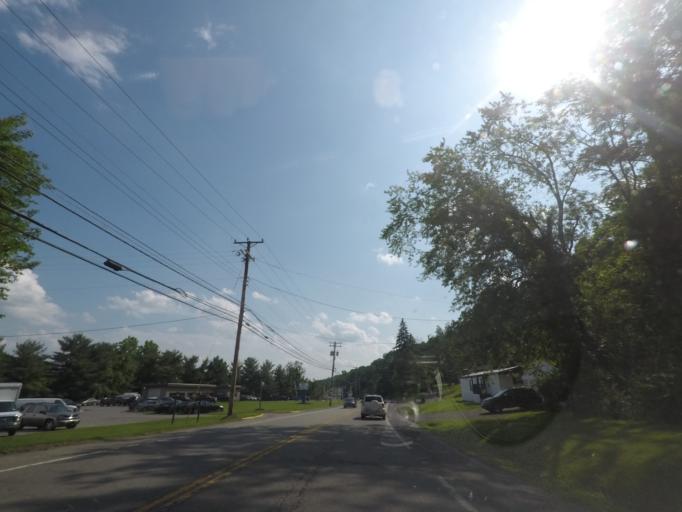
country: US
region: New York
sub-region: Ulster County
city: Marlboro
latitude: 41.5958
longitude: -73.9759
